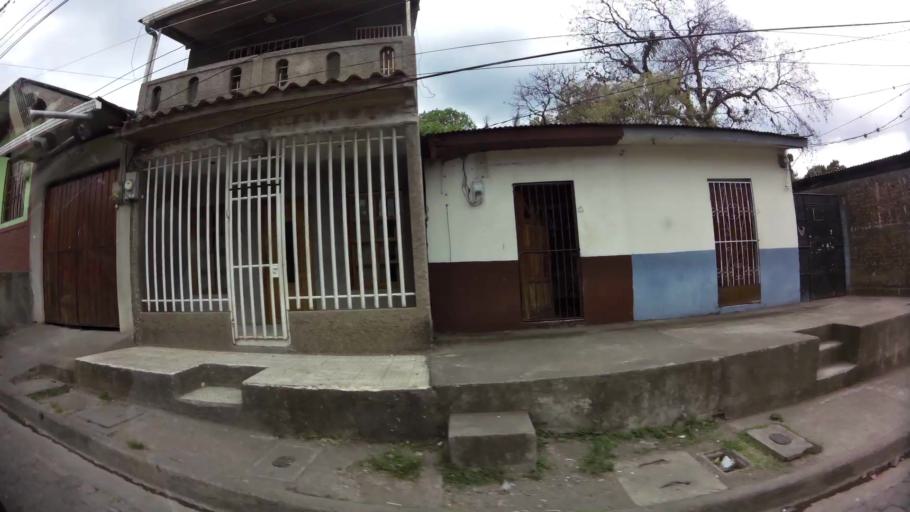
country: NI
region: Matagalpa
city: Matagalpa
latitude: 12.9330
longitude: -85.9177
